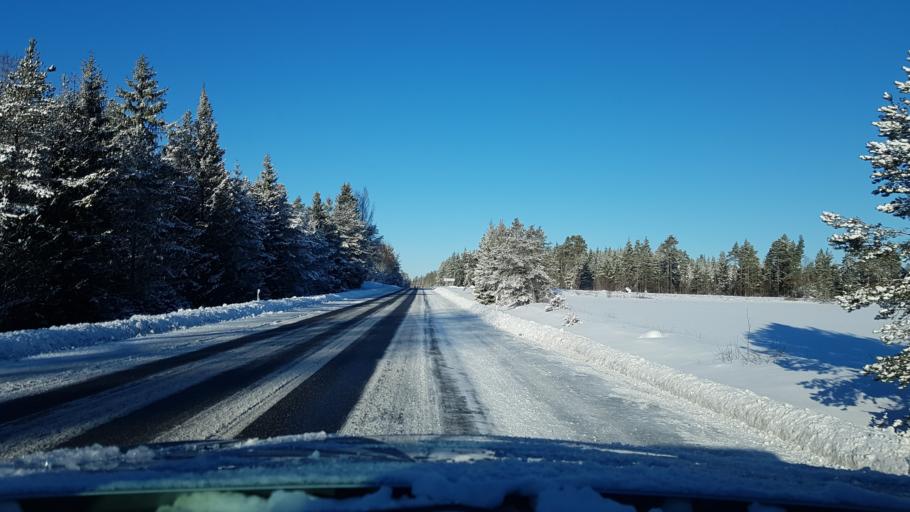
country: EE
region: Hiiumaa
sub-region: Kaerdla linn
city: Kardla
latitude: 58.9695
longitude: 22.8283
